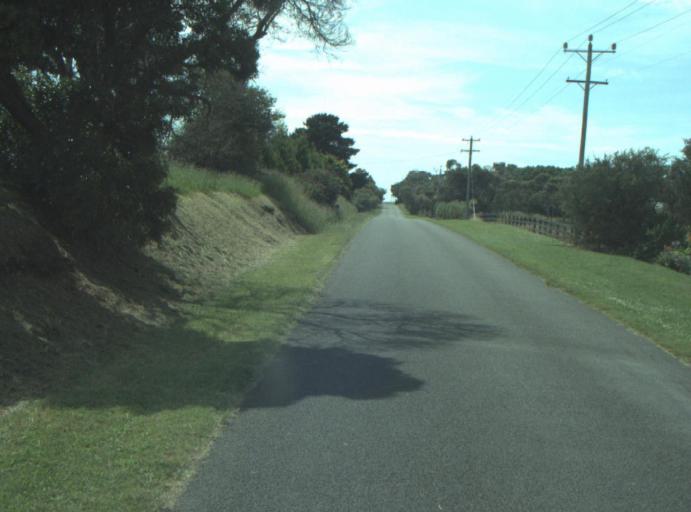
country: AU
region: Victoria
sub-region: Greater Geelong
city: Clifton Springs
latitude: -38.1472
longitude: 144.6030
